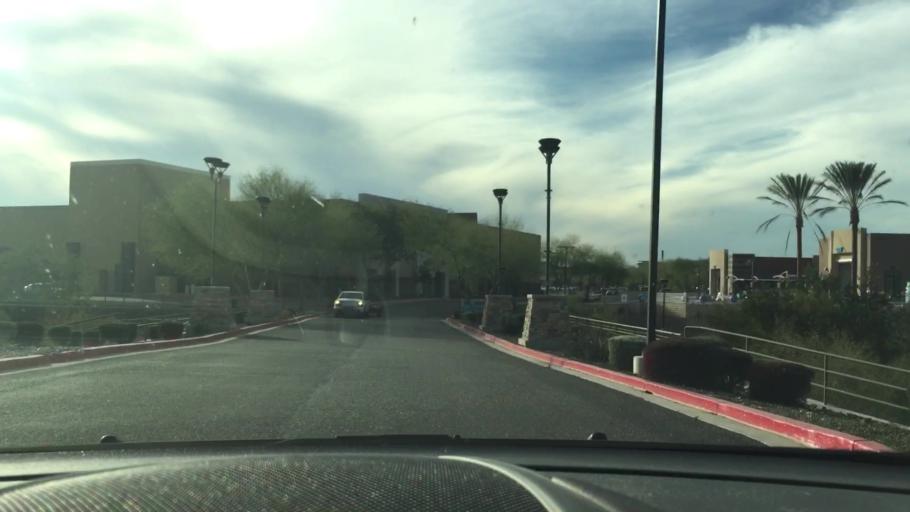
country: US
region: Arizona
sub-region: Maricopa County
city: Sun City West
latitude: 33.7146
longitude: -112.2721
